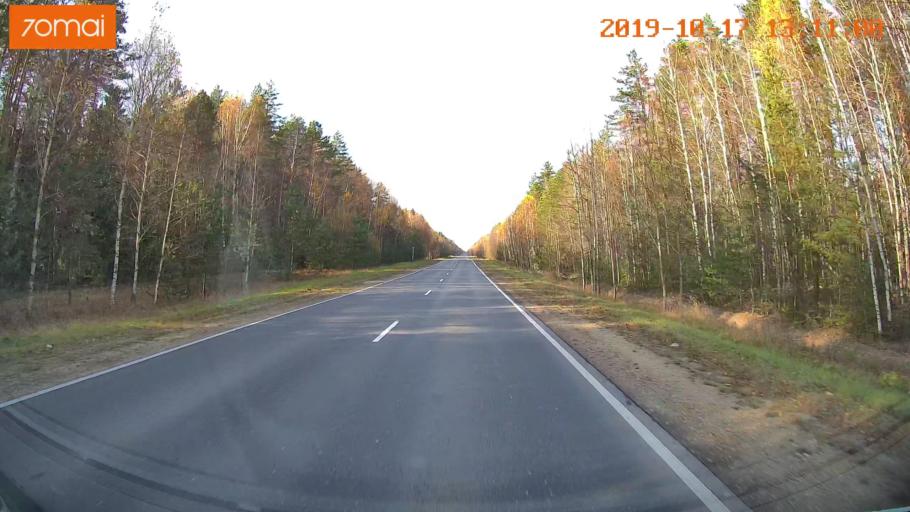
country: RU
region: Rjazan
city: Syntul
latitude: 55.0239
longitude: 41.2451
